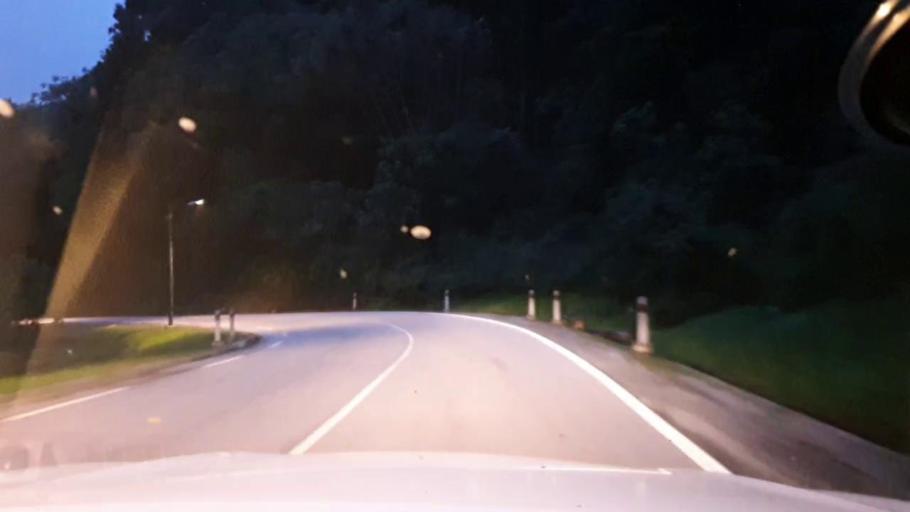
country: RW
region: Southern Province
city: Nzega
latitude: -2.5334
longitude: 29.3875
